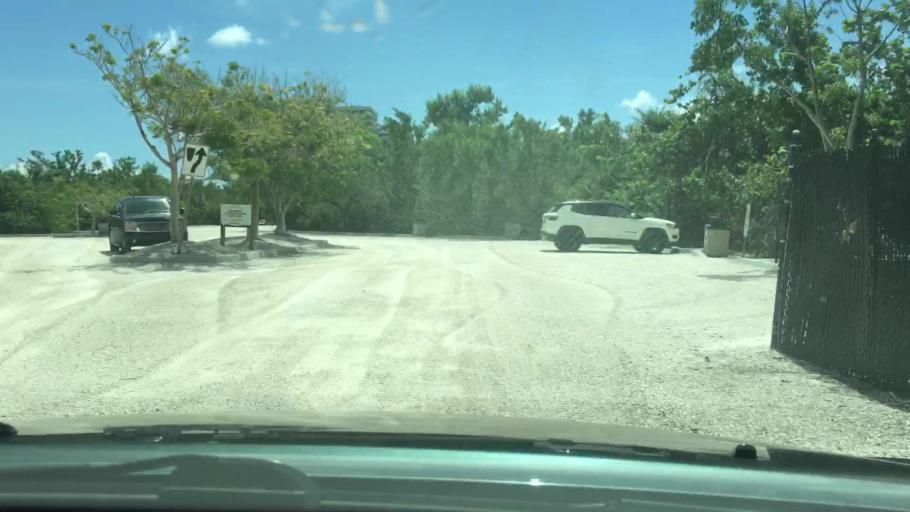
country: US
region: Florida
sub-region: Collier County
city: Marco
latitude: 25.9484
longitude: -81.7429
